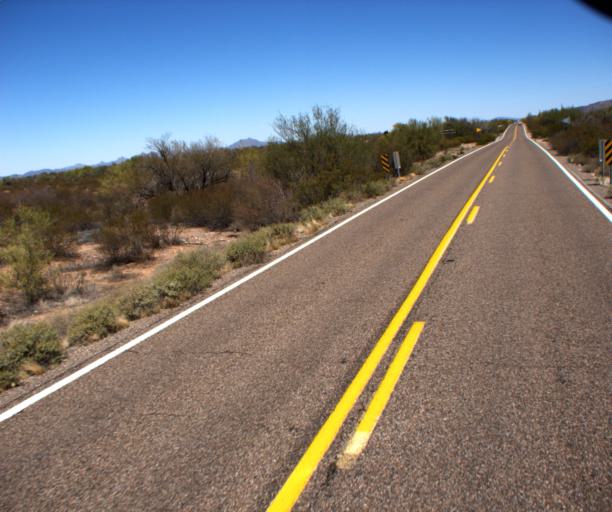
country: US
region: Arizona
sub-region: Pima County
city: Ajo
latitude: 32.1343
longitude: -112.7671
